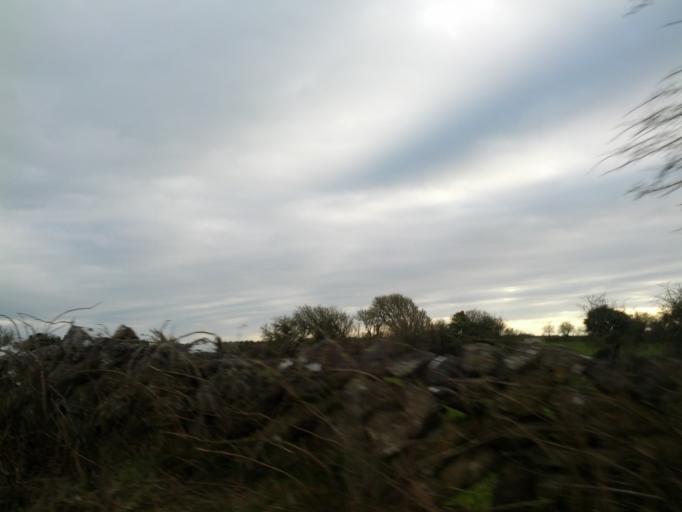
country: IE
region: Connaught
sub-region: County Galway
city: Gort
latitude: 53.1556
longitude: -8.8653
